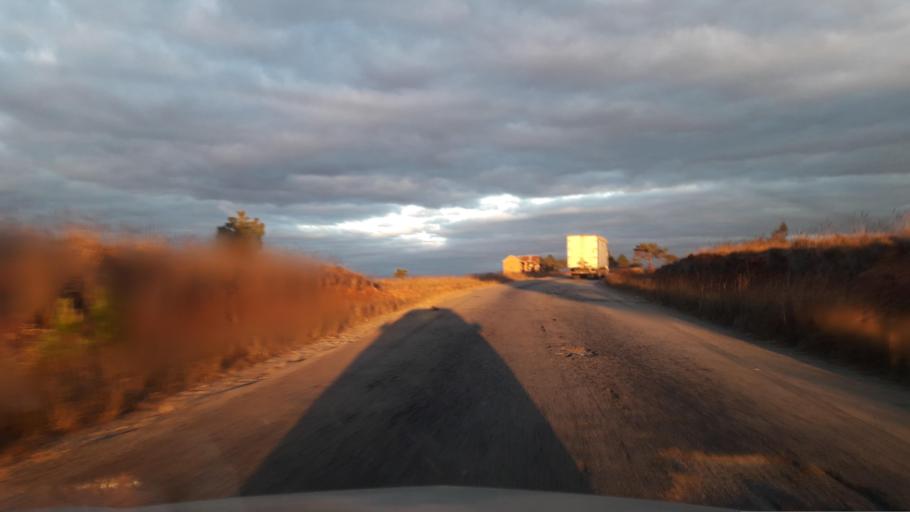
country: MG
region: Analamanga
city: Ankazobe
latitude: -17.8851
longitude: 47.0814
